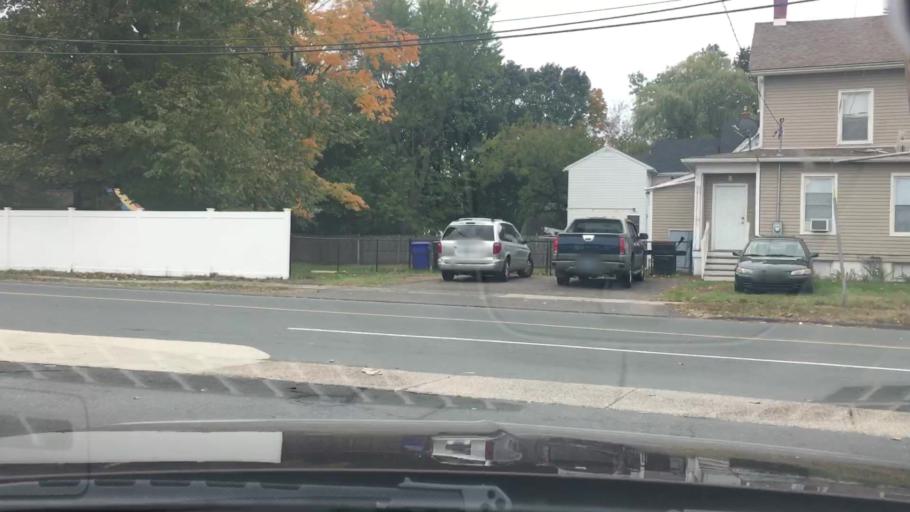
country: US
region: Connecticut
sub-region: Hartford County
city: East Hartford
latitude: 41.7616
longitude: -72.6342
